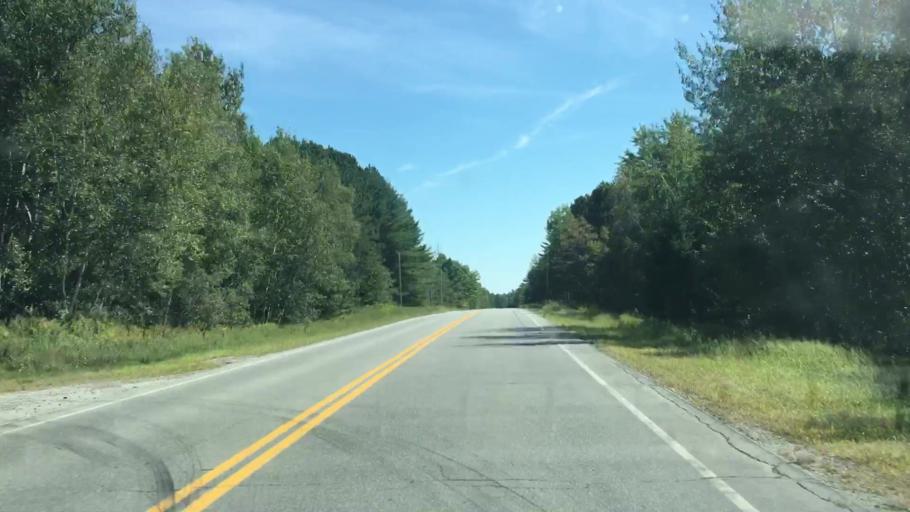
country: US
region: Maine
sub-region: Piscataquis County
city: Milo
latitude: 45.2279
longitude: -68.9324
